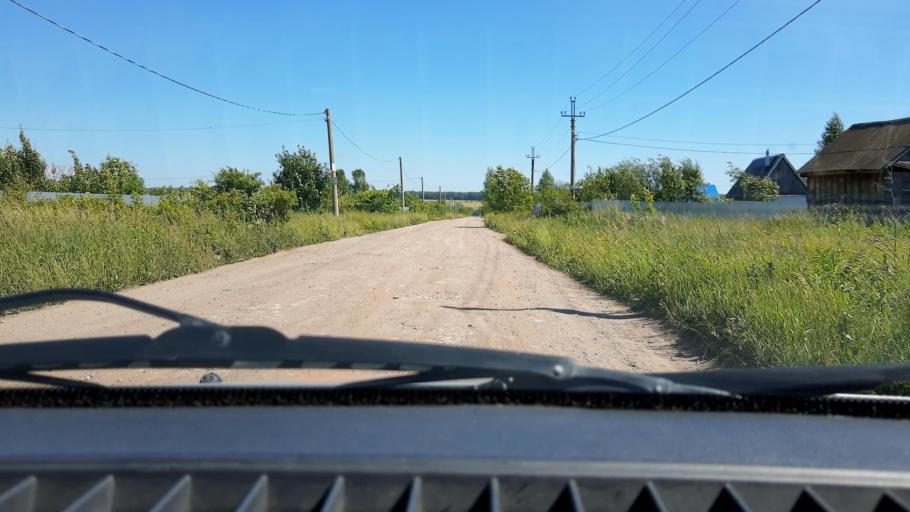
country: RU
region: Bashkortostan
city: Avdon
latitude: 54.5471
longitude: 55.7170
